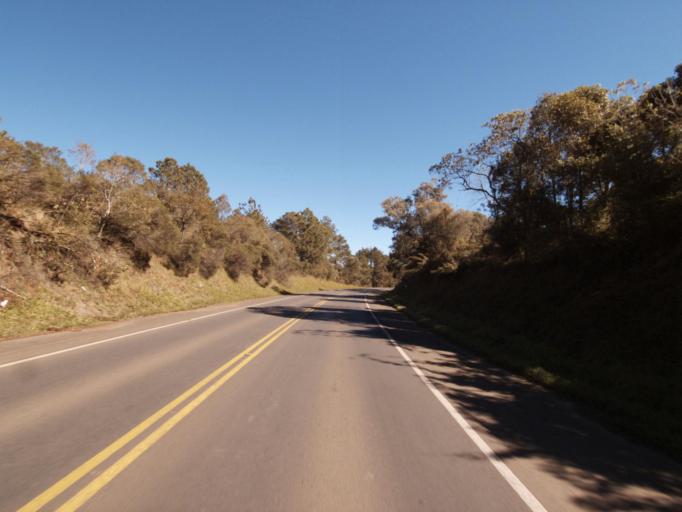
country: BR
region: Santa Catarina
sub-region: Joacaba
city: Joacaba
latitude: -26.9761
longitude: -51.7719
